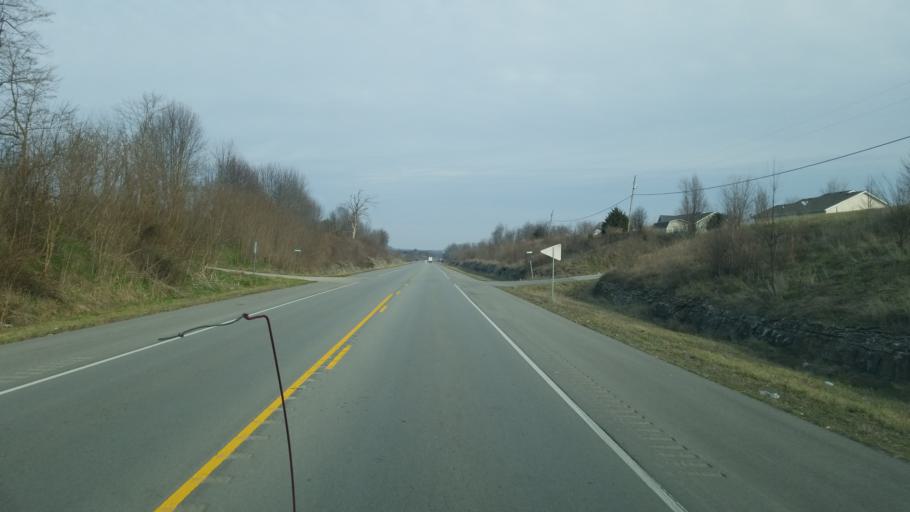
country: US
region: Kentucky
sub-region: Boyle County
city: Junction City
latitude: 37.5224
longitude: -84.8059
